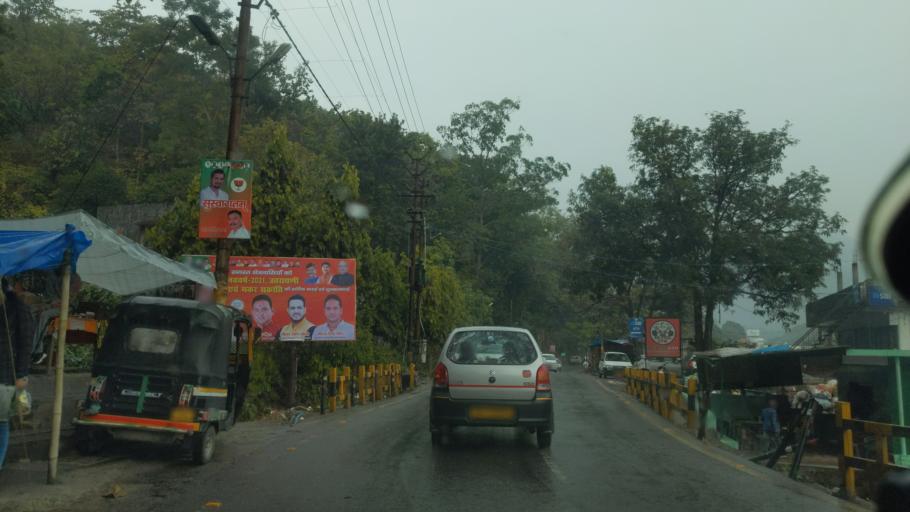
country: IN
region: Uttarakhand
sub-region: Naini Tal
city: Haldwani
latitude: 29.2823
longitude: 79.5449
